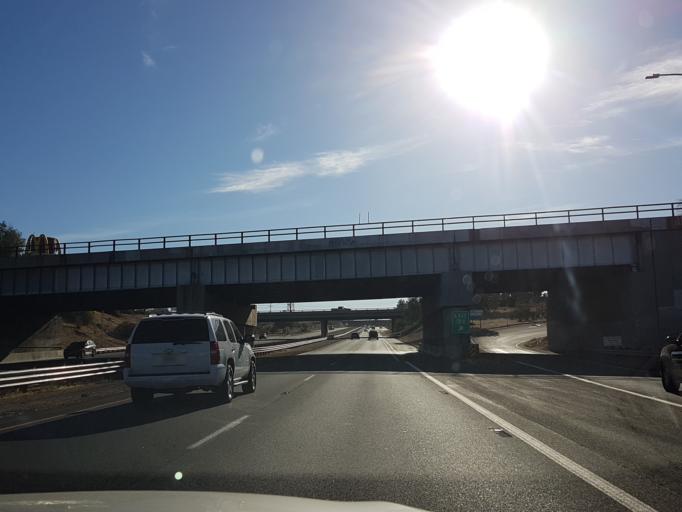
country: US
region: California
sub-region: San Bernardino County
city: Barstow
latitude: 34.8932
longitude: -116.9988
